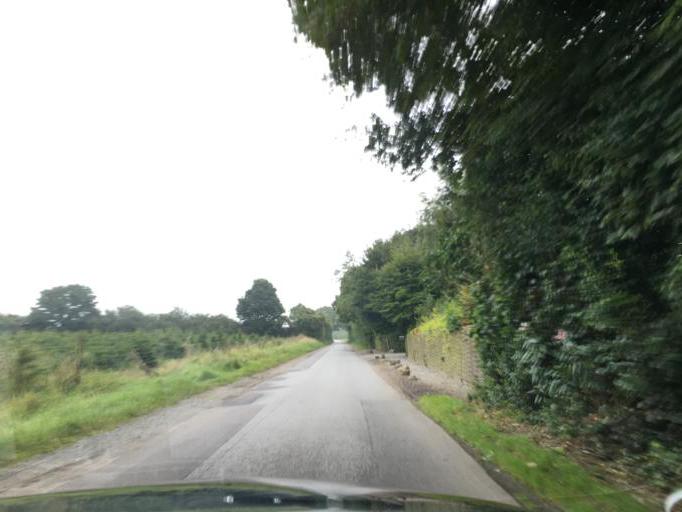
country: DK
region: South Denmark
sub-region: Kolding Kommune
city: Kolding
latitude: 55.5656
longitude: 9.4728
